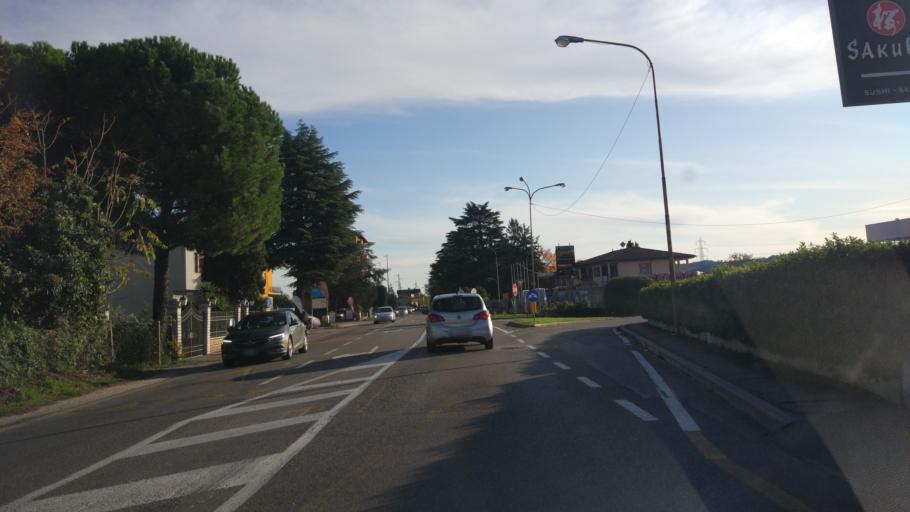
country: IT
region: Veneto
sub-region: Provincia di Verona
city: Volargne
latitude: 45.5242
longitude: 10.8182
